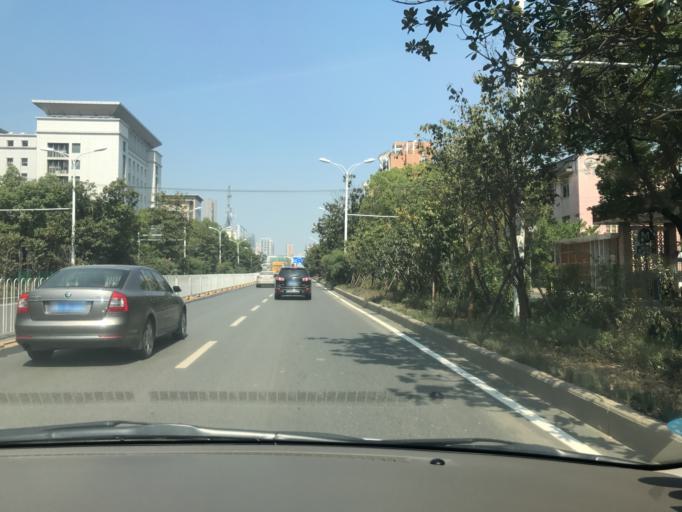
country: CN
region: Hubei
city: Shilipu
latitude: 30.5609
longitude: 114.2179
